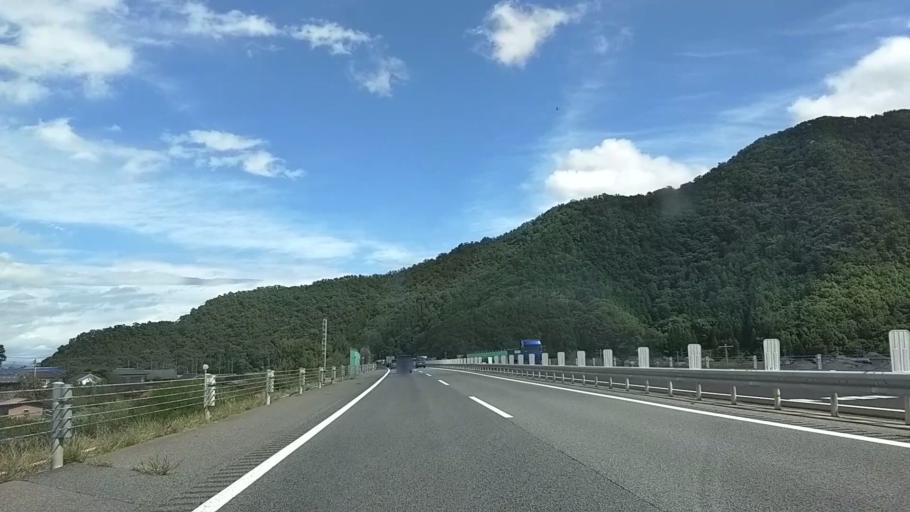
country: JP
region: Nagano
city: Suzaka
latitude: 36.6111
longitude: 138.2539
